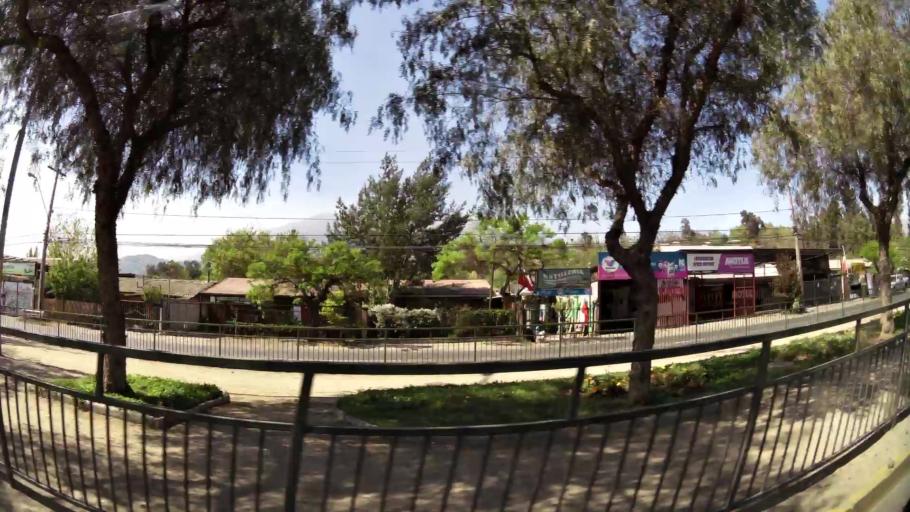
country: CL
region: Santiago Metropolitan
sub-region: Provincia de Cordillera
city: Puente Alto
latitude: -33.5768
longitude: -70.5531
